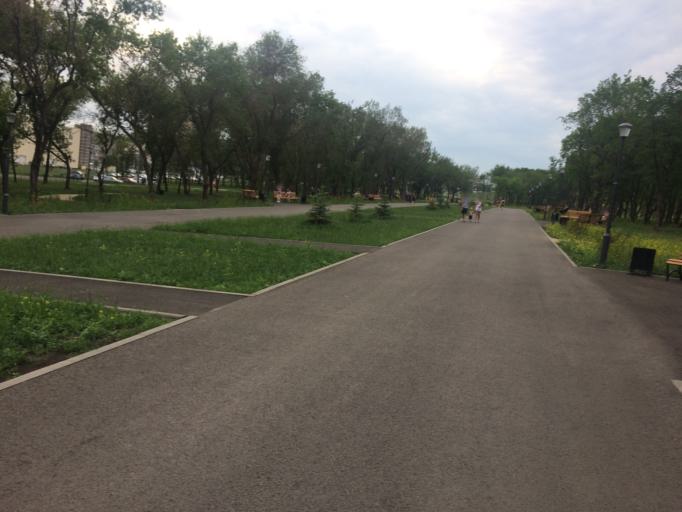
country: RU
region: Chelyabinsk
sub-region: Gorod Magnitogorsk
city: Magnitogorsk
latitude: 53.4024
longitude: 58.9922
